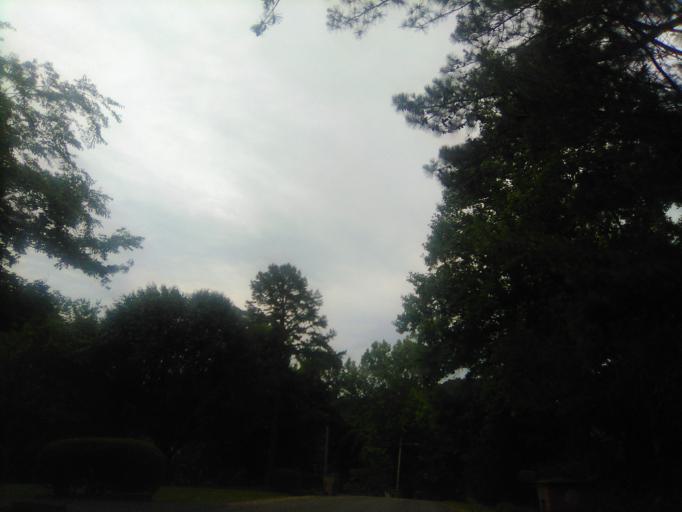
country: US
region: Tennessee
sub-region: Davidson County
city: Belle Meade
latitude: 36.1058
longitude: -86.8927
